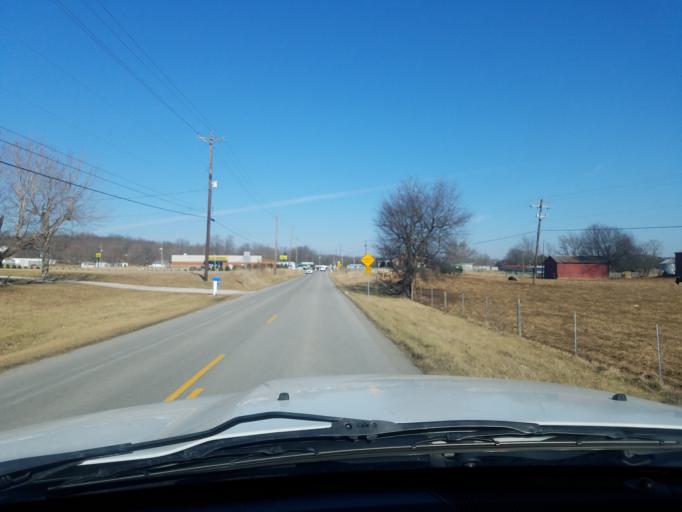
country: US
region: Kentucky
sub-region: Hardin County
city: Elizabethtown
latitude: 37.5745
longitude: -86.0369
